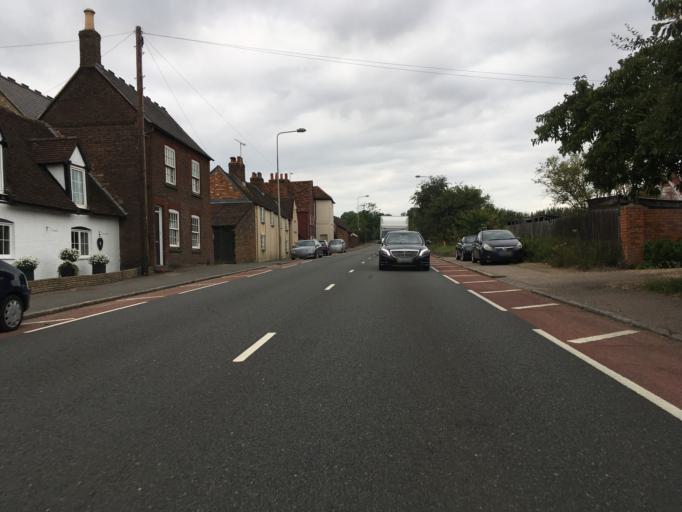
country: GB
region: England
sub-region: Central Bedfordshire
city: Hockliffe
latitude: 51.9331
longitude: -0.5895
